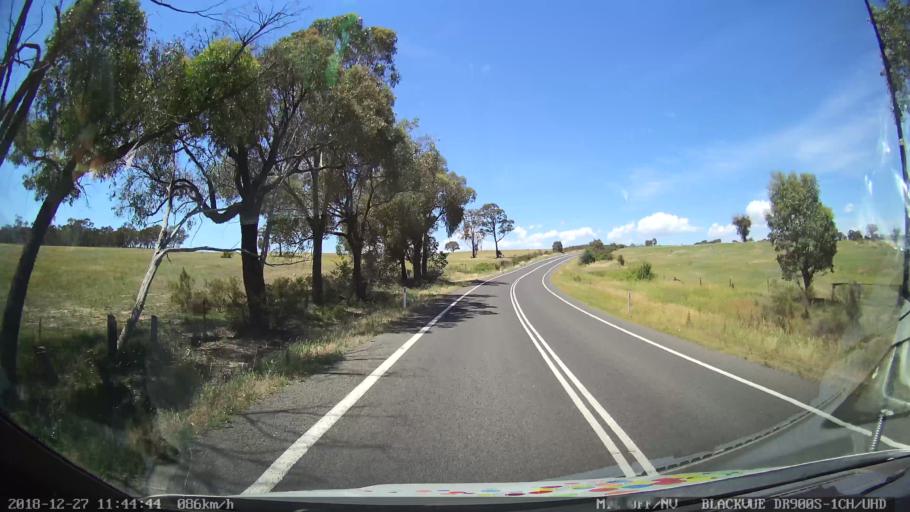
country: AU
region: New South Wales
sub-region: Bathurst Regional
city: Perthville
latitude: -33.5755
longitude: 149.4762
